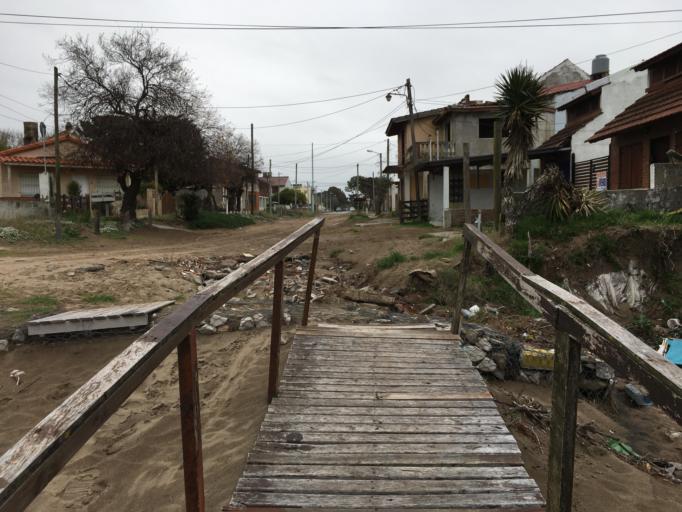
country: AR
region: Buenos Aires
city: Mar del Tuyu
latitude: -36.5546
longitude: -56.6883
